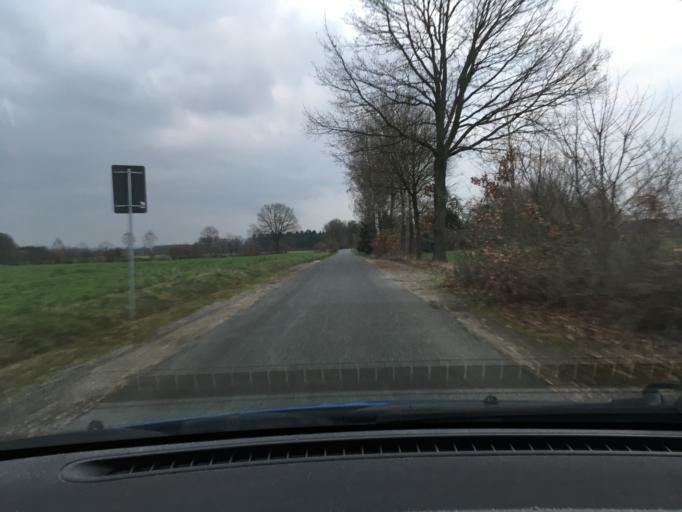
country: DE
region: Lower Saxony
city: Walsrode
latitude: 52.8394
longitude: 9.5631
